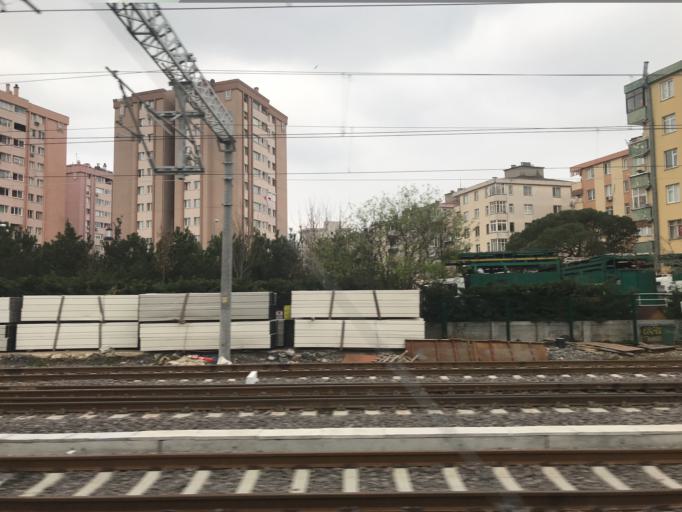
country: TR
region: Istanbul
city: Maltepe
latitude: 40.9191
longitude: 29.1373
